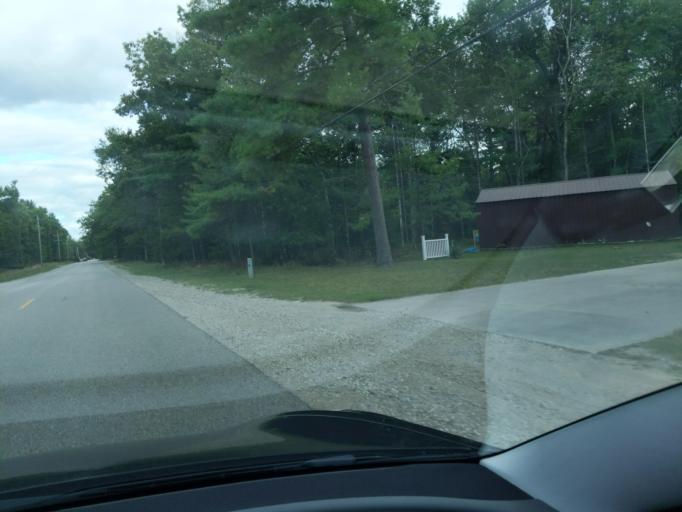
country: US
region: Michigan
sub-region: Kalkaska County
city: Rapid City
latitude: 44.8492
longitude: -85.3119
